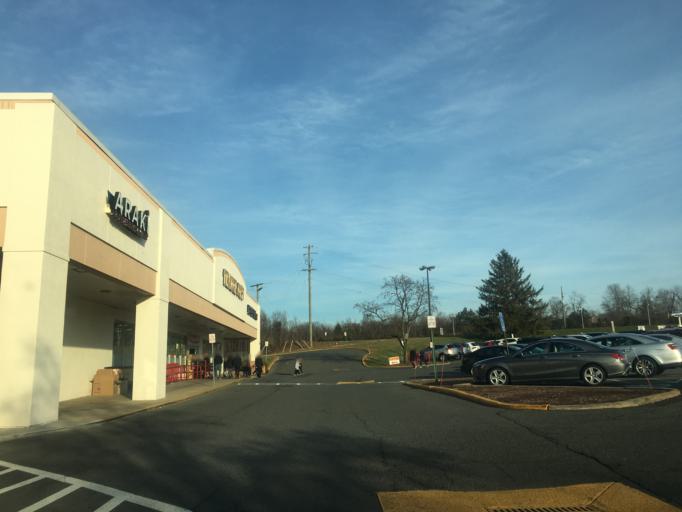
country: US
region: Virginia
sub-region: Fairfax County
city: Centreville
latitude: 38.8401
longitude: -77.4330
